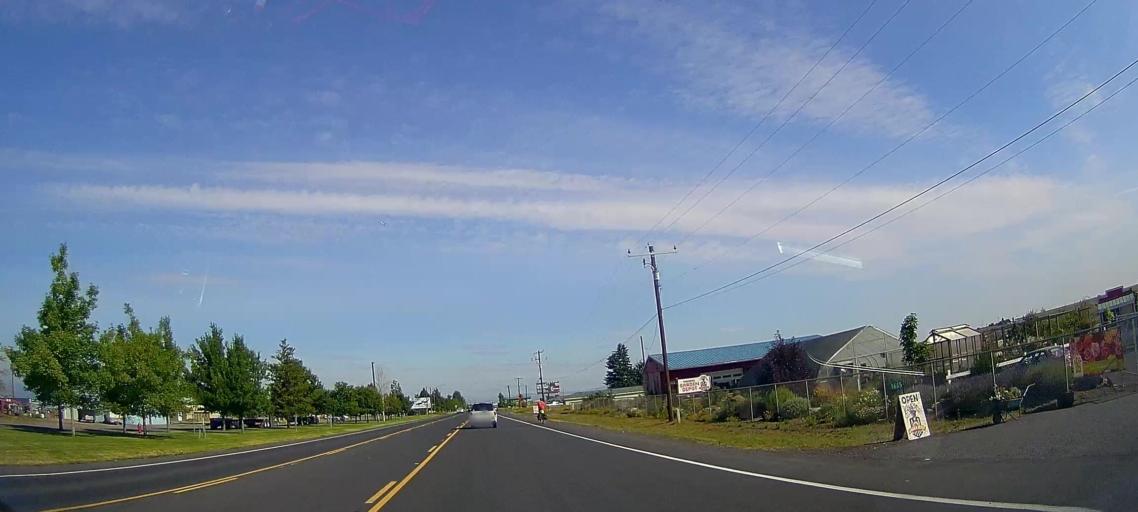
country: US
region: Oregon
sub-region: Jefferson County
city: Madras
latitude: 44.6592
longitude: -121.1319
